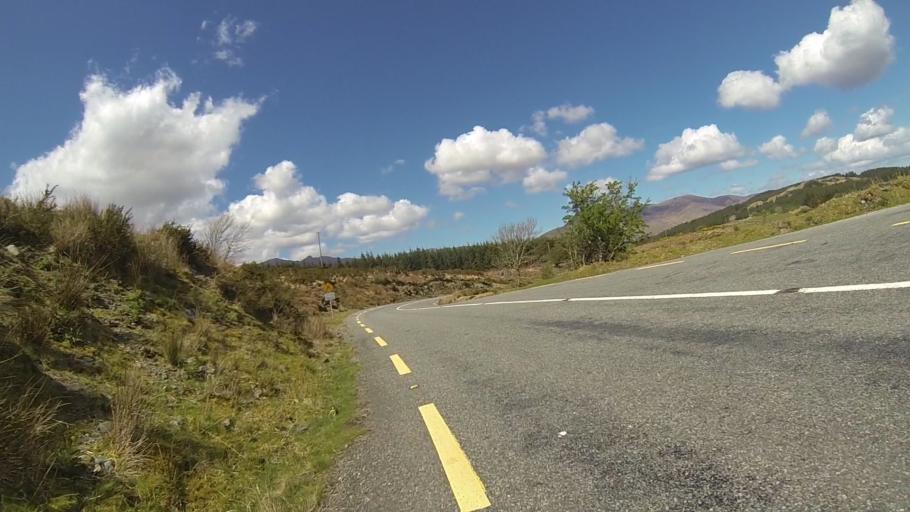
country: IE
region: Munster
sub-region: Ciarrai
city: Kenmare
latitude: 51.9523
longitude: -9.6268
